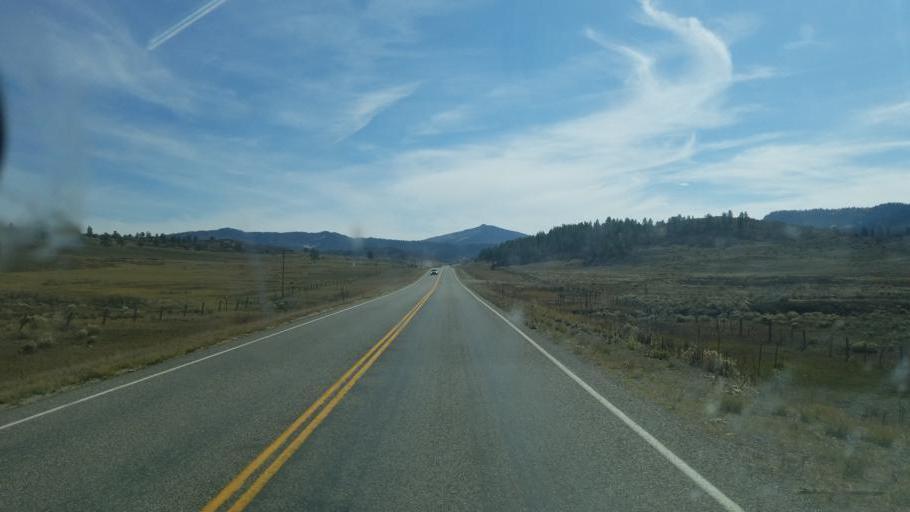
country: US
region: New Mexico
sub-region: Rio Arriba County
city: Dulce
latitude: 37.0225
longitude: -106.8186
